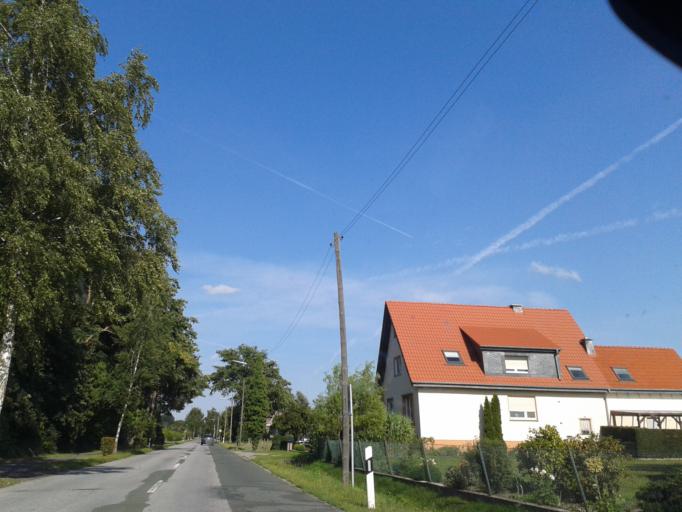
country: DE
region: North Rhine-Westphalia
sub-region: Regierungsbezirk Detmold
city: Paderborn
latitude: 51.7599
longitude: 8.7487
